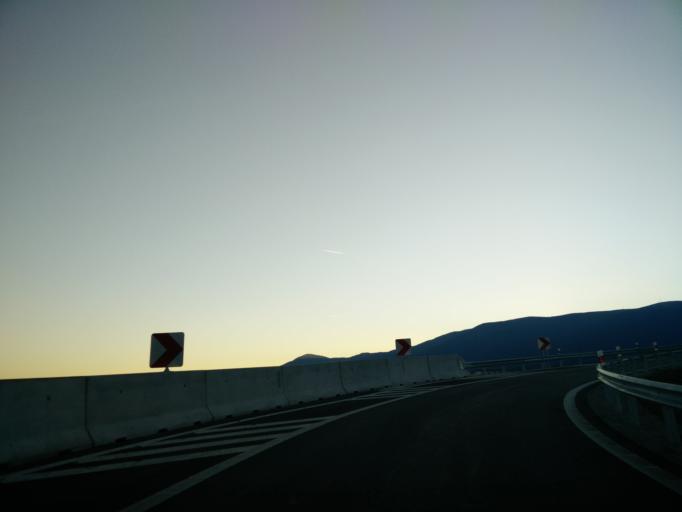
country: SK
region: Zilinsky
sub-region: Okres Martin
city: Martin
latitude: 49.0939
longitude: 18.9506
